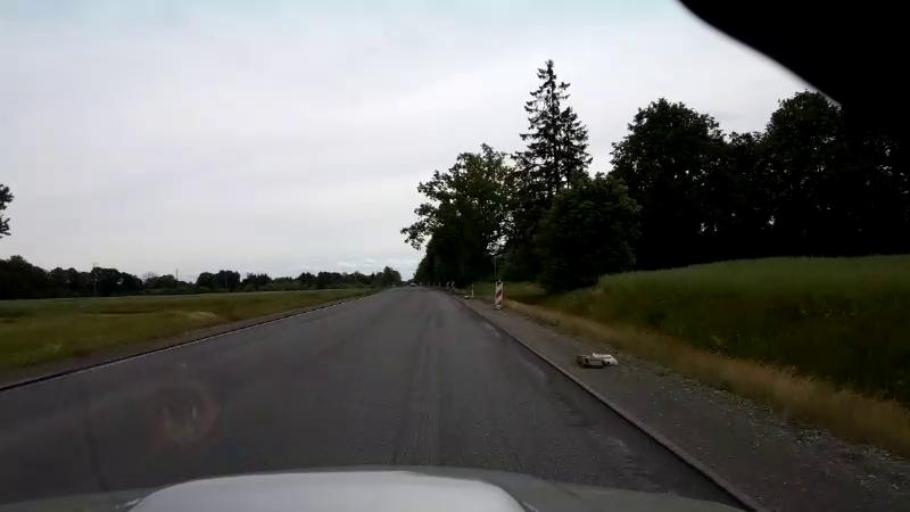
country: LV
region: Bauskas Rajons
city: Bauska
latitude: 56.3231
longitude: 24.3140
